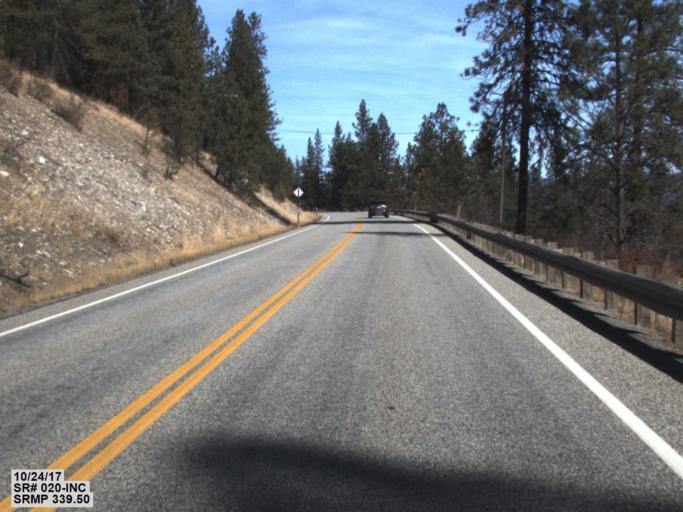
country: US
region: Washington
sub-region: Stevens County
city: Kettle Falls
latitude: 48.5956
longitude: -118.1451
